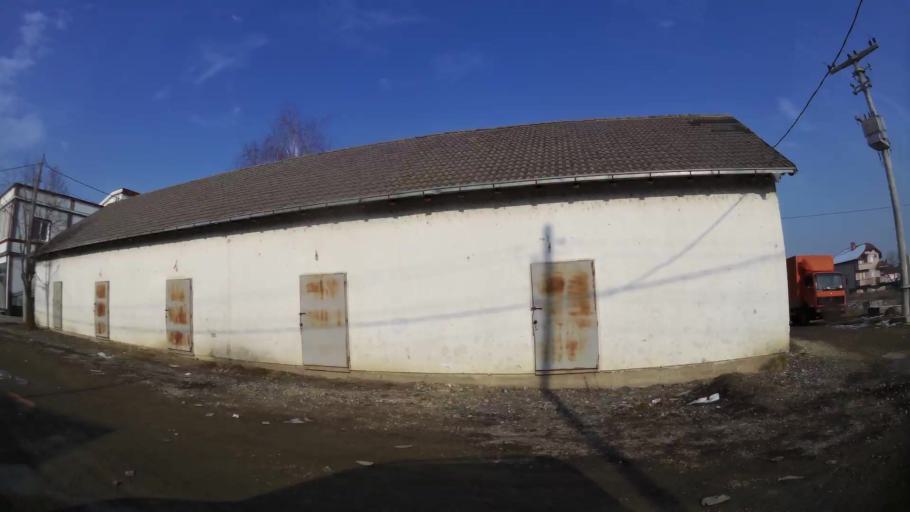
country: MK
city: Creshevo
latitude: 42.0209
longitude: 21.5024
